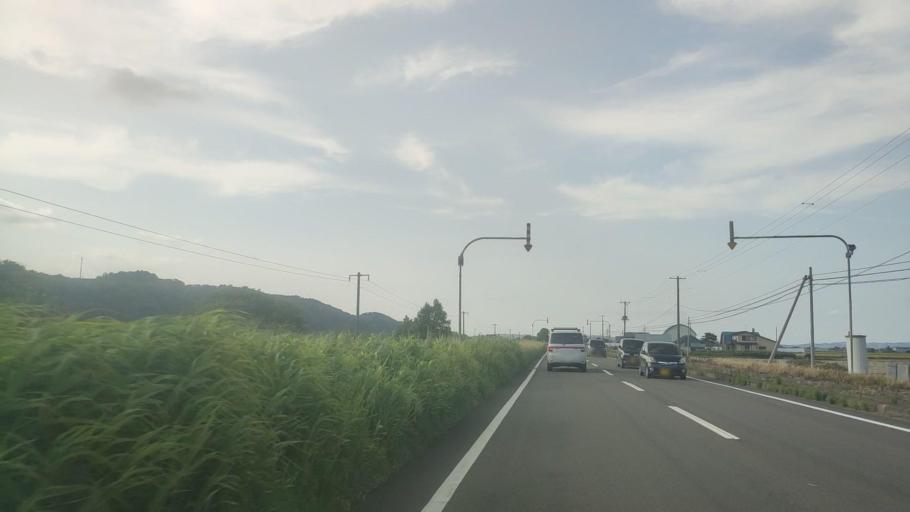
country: JP
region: Hokkaido
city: Iwamizawa
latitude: 42.9911
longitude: 141.7909
